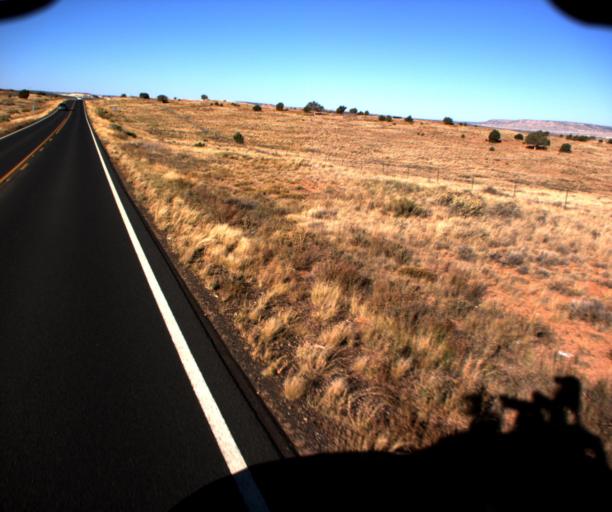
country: US
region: Arizona
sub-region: Apache County
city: Ganado
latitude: 35.7858
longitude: -109.6989
